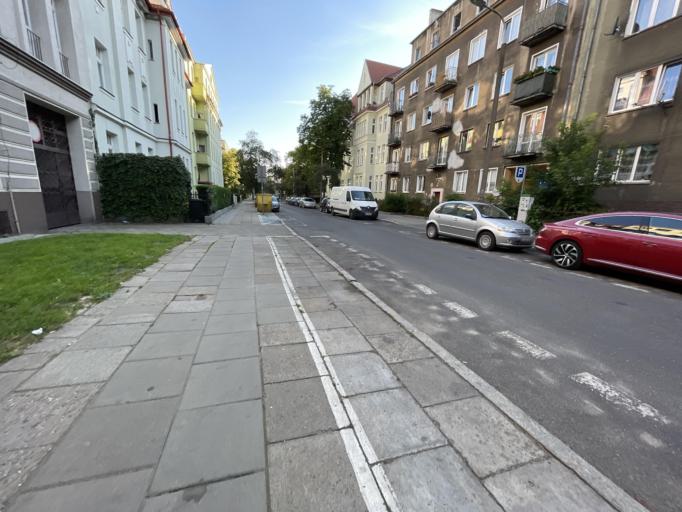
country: PL
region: Kujawsko-Pomorskie
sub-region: Bydgoszcz
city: Bydgoszcz
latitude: 53.1325
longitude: 18.0157
